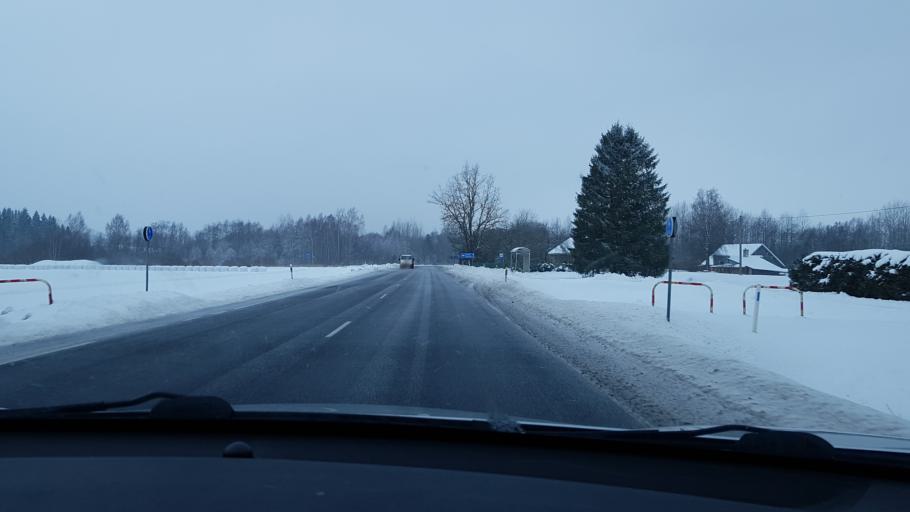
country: EE
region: Jaervamaa
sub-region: Tueri vald
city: Sarevere
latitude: 58.7682
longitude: 25.4178
